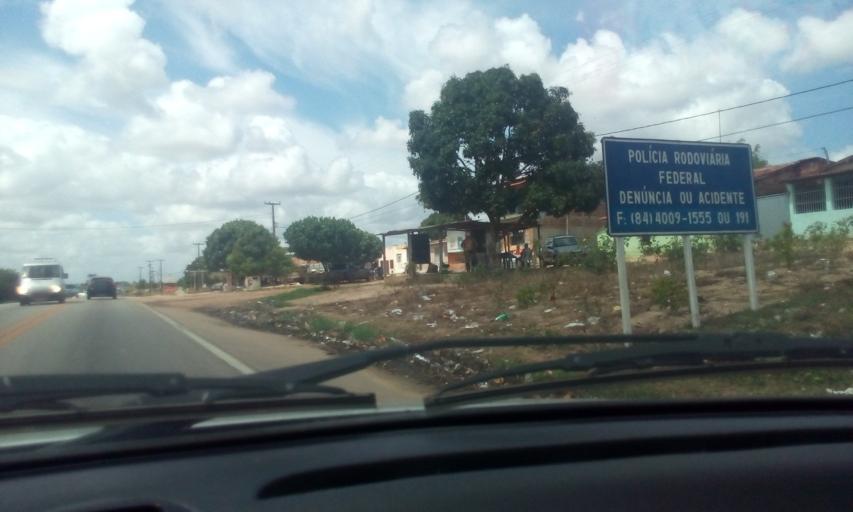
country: BR
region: Rio Grande do Norte
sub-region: Macaiba
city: Macaiba
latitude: -5.9329
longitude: -35.5453
